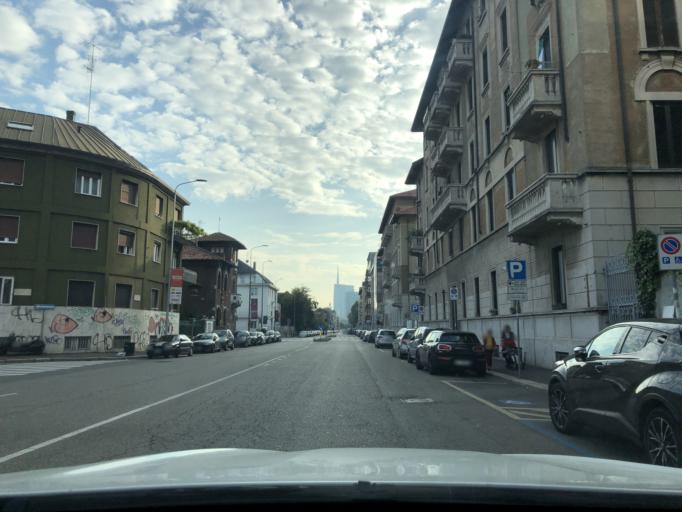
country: IT
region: Lombardy
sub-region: Citta metropolitana di Milano
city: Milano
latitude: 45.4997
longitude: 9.1987
